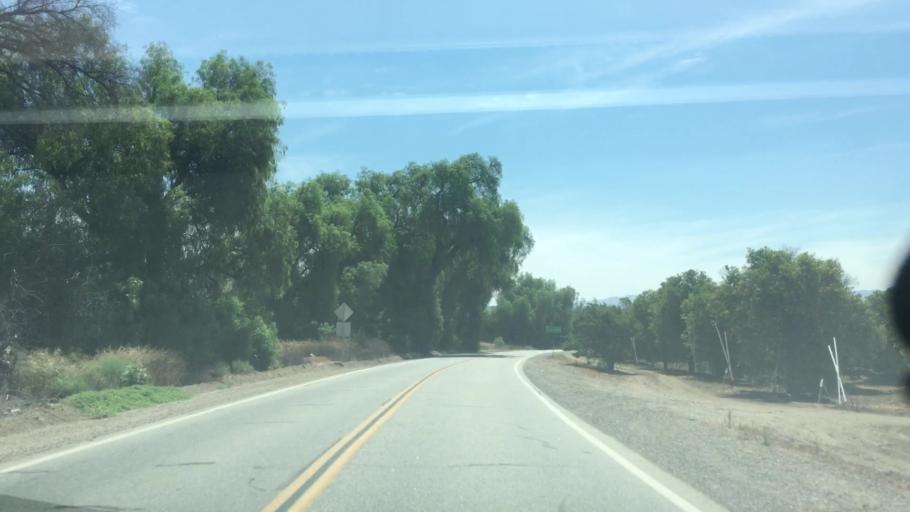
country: US
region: California
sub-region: Ventura County
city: Fillmore
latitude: 34.4085
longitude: -118.9377
